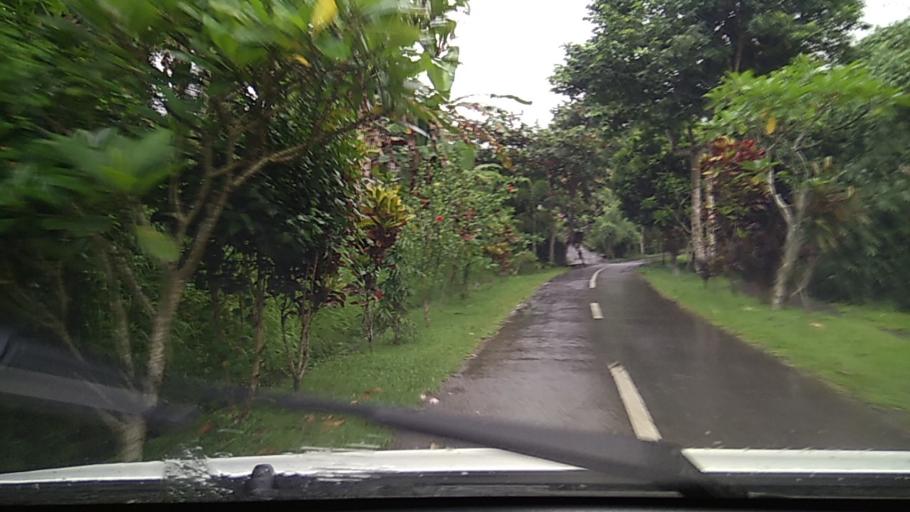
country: ID
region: Bali
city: Tiyingtali Kelod
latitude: -8.4085
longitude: 115.6261
